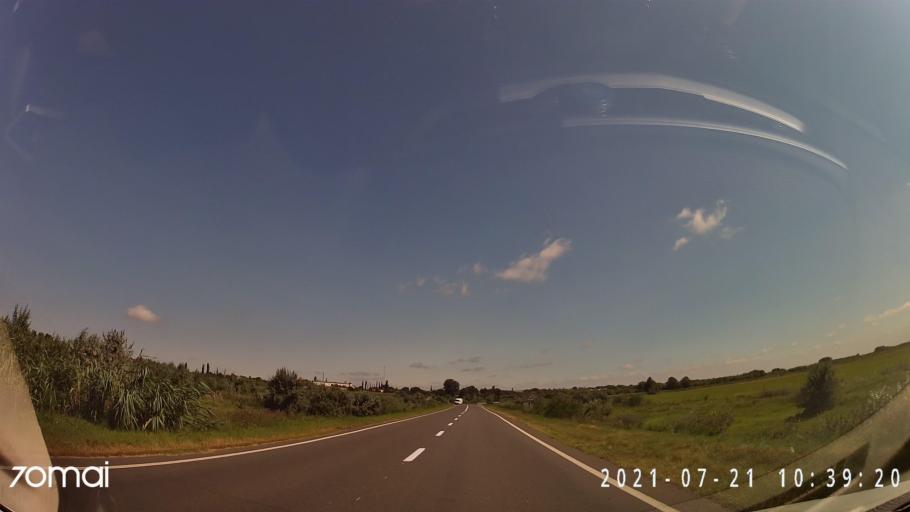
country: RO
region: Tulcea
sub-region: Oras Isaccea
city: Isaccea
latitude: 45.3082
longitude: 28.4393
